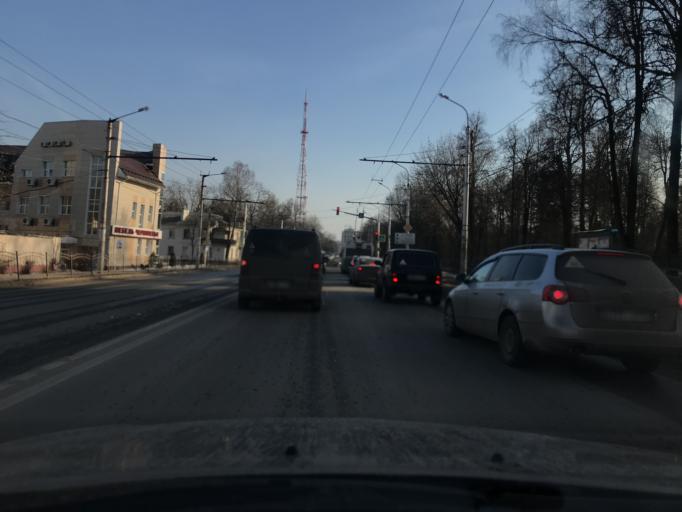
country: RU
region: Kaluga
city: Kaluga
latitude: 54.5267
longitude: 36.2614
